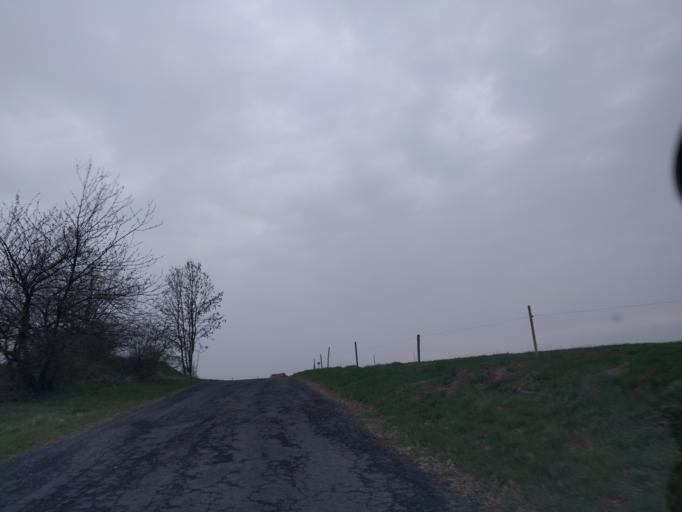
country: CZ
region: Karlovarsky
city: Bochov
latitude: 50.1176
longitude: 13.0867
